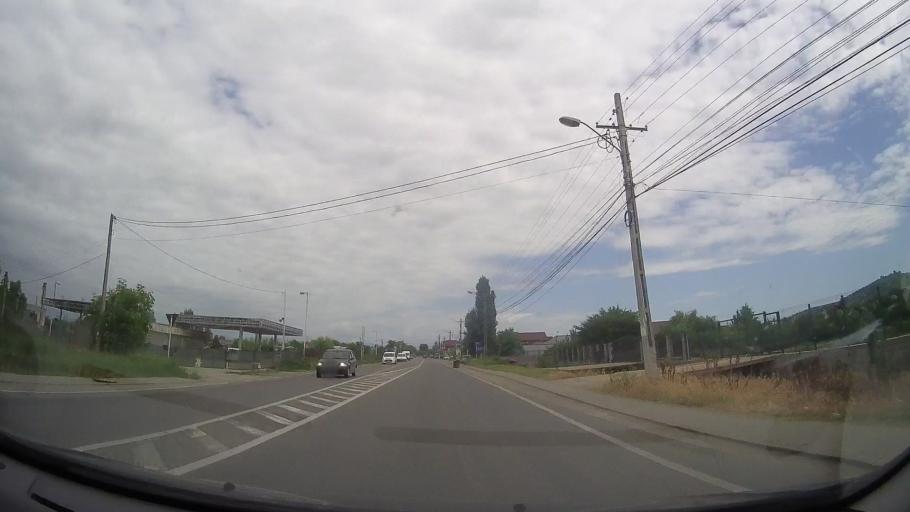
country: RO
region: Prahova
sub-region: Comuna Lipanesti
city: Sipotu
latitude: 45.0271
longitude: 26.0187
